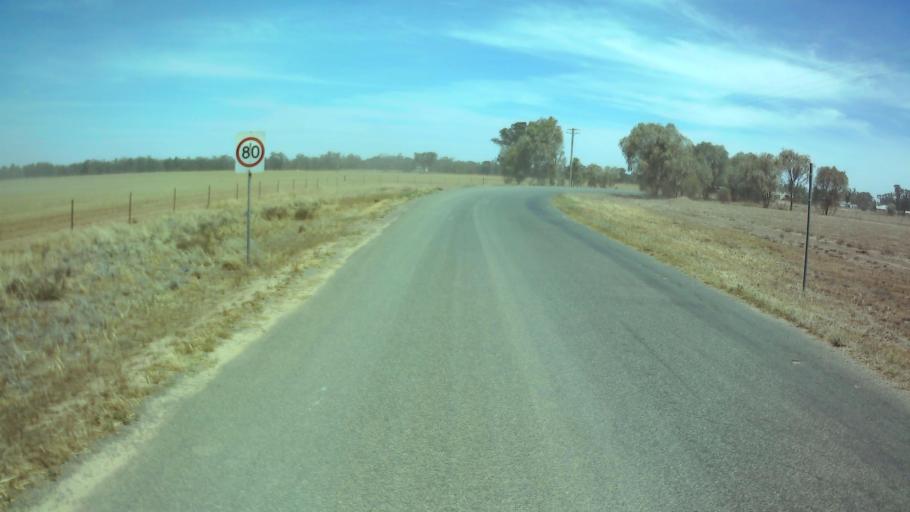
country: AU
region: New South Wales
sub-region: Weddin
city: Grenfell
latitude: -33.8357
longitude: 147.7465
